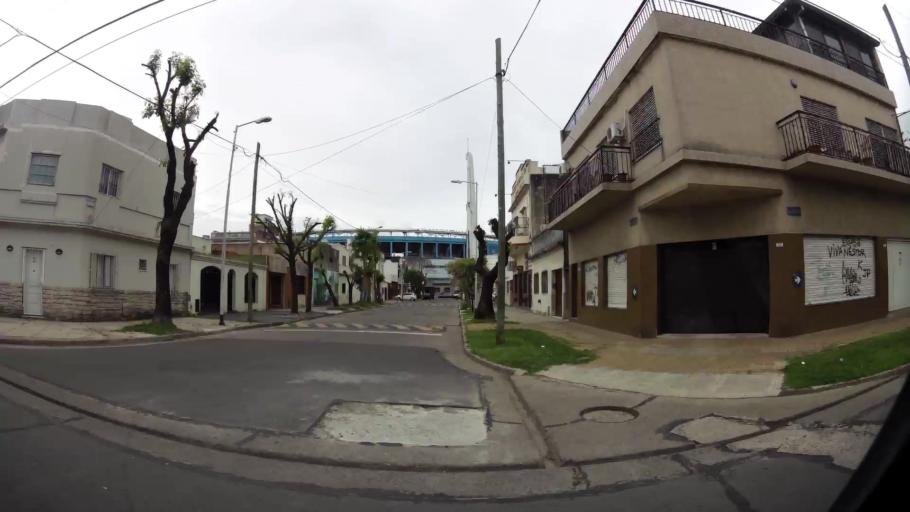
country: AR
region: Buenos Aires
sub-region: Partido de Avellaneda
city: Avellaneda
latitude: -34.6661
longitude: -58.3709
